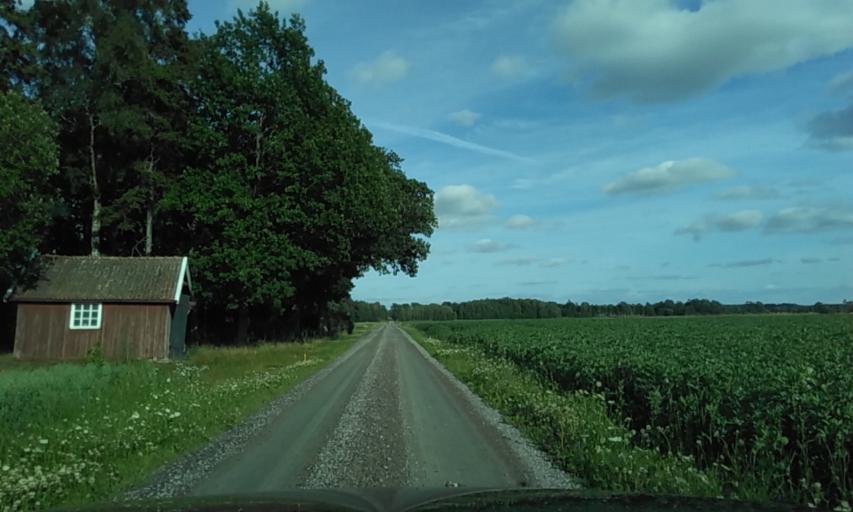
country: SE
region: Vaestra Goetaland
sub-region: Grastorps Kommun
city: Graestorp
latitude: 58.3752
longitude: 12.8206
